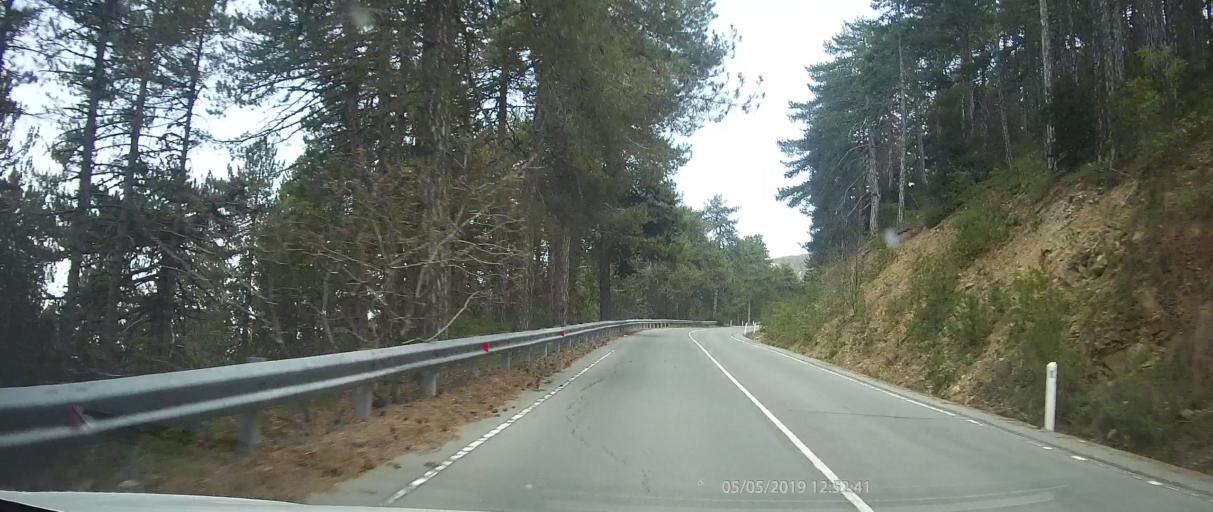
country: CY
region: Lefkosia
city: Kakopetria
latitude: 34.9522
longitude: 32.8378
